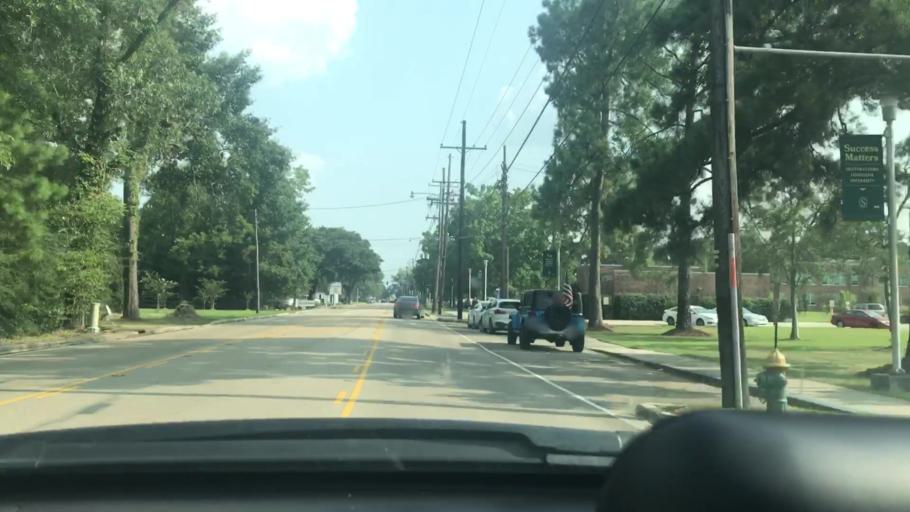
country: US
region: Louisiana
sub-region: Tangipahoa Parish
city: Hammond
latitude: 30.5146
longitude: -90.4657
